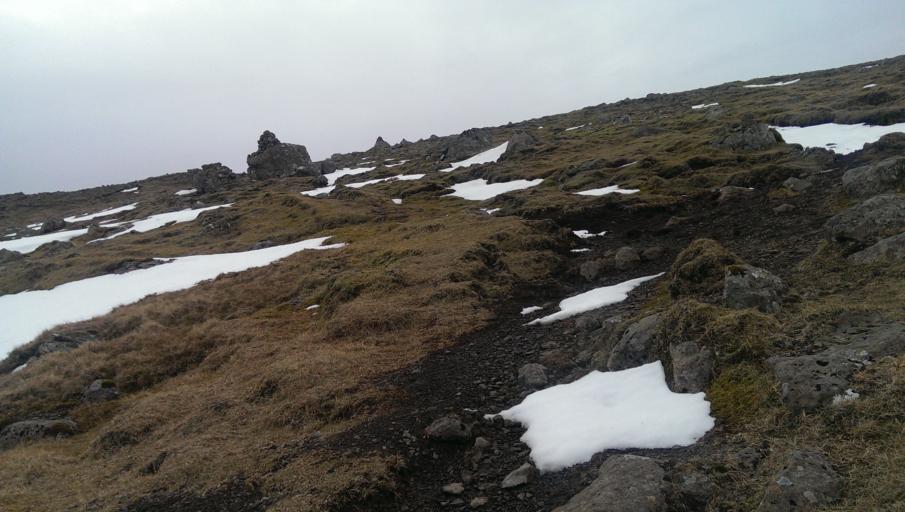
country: FO
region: Streymoy
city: Kollafjordhur
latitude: 62.0308
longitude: -6.8837
